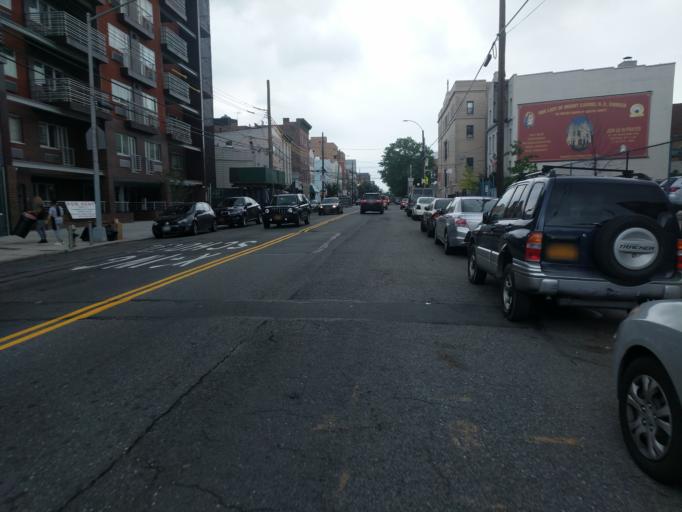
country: US
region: New York
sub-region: Queens County
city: Long Island City
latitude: 40.7717
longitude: -73.9240
